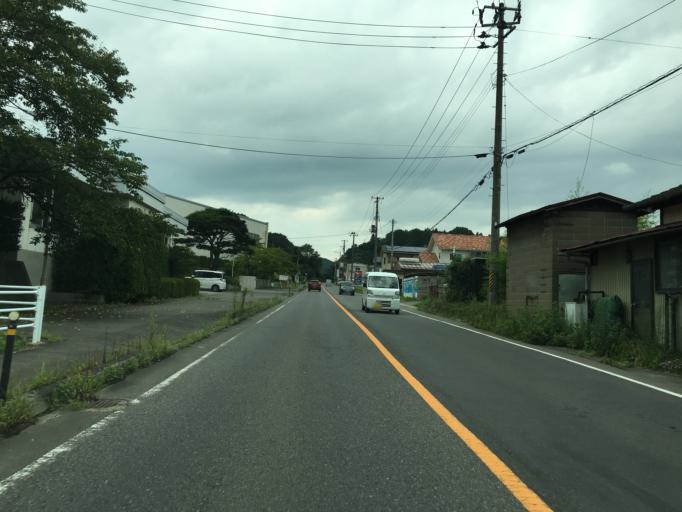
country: JP
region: Fukushima
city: Nihommatsu
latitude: 37.5788
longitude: 140.4168
